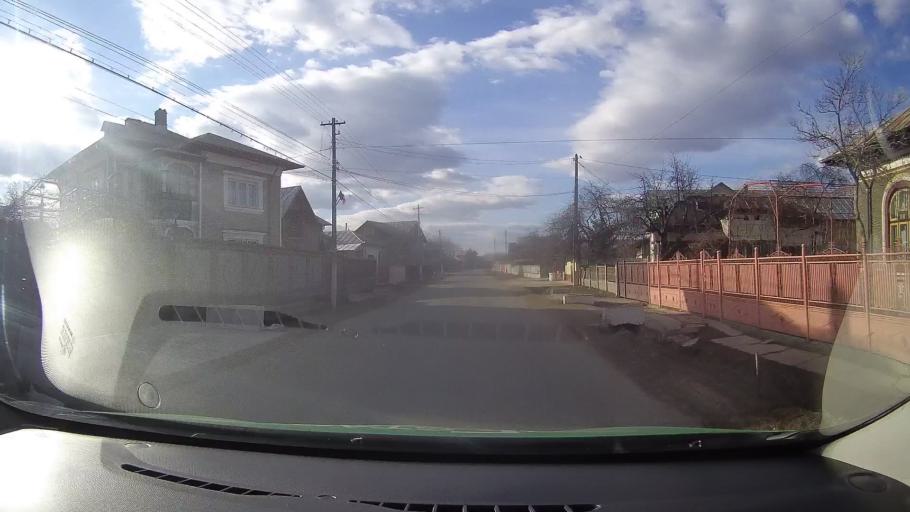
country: RO
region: Dambovita
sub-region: Comuna Comisani
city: Lazuri
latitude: 44.8757
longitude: 25.5194
